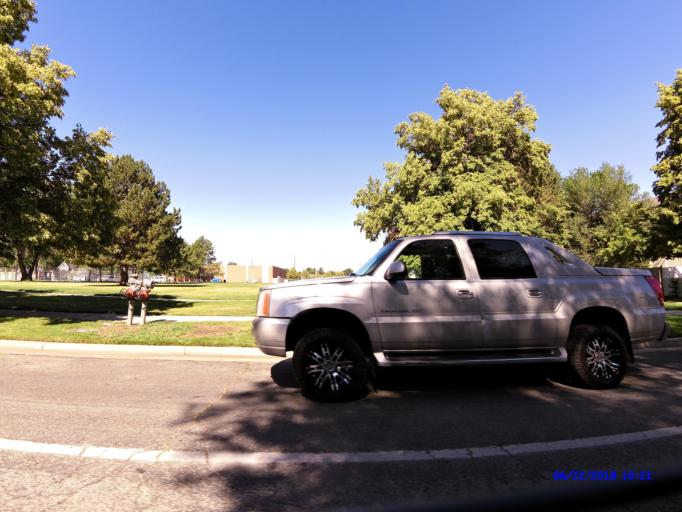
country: US
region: Utah
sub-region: Weber County
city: Ogden
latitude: 41.2153
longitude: -111.9735
